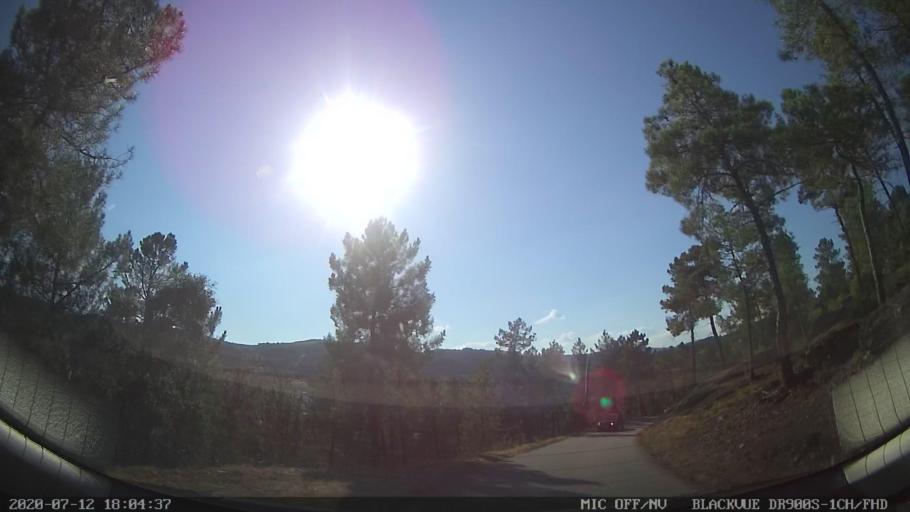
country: PT
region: Viseu
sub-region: Sao Joao da Pesqueira
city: Sao Joao da Pesqueira
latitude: 41.2508
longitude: -7.4281
